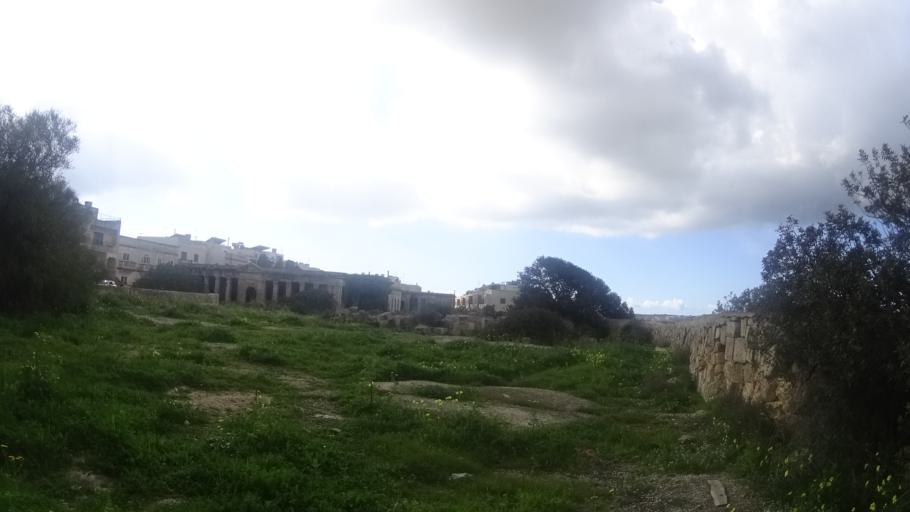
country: MT
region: L-Imtarfa
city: Imtarfa
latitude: 35.8911
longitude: 14.3943
